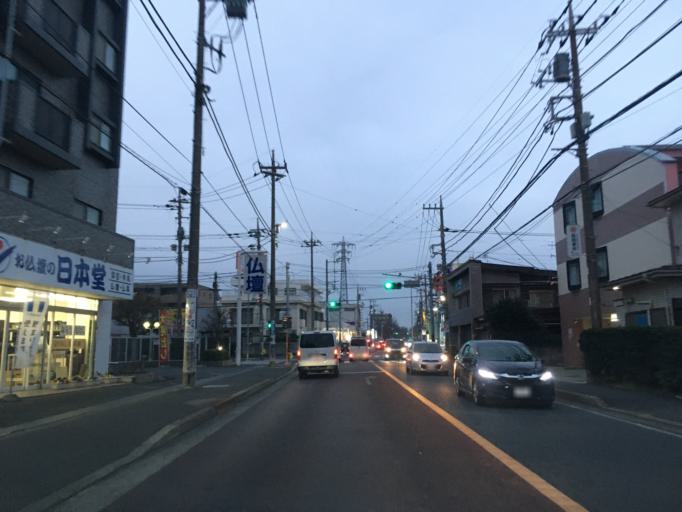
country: JP
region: Kanagawa
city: Minami-rinkan
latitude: 35.4750
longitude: 139.4651
